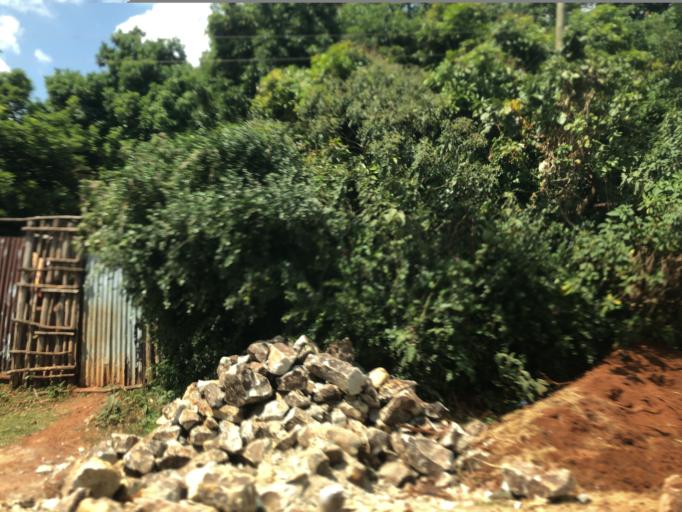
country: ET
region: Southern Nations, Nationalities, and People's Region
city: Boditi
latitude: 6.8704
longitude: 37.7674
